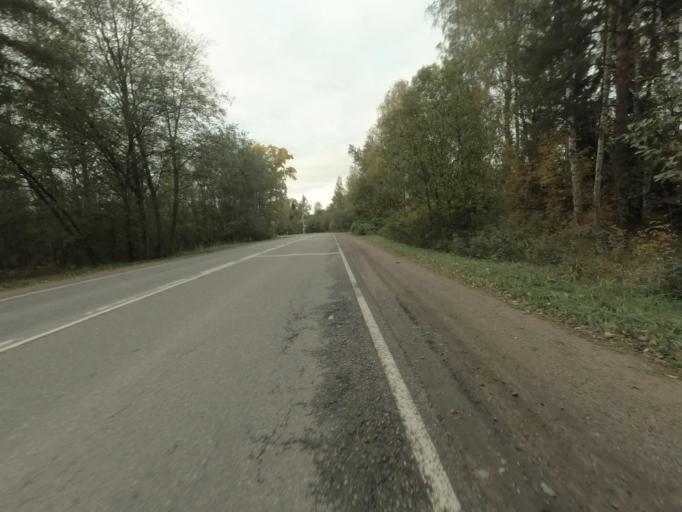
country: RU
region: Leningrad
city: Pavlovo
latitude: 59.7851
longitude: 30.9697
